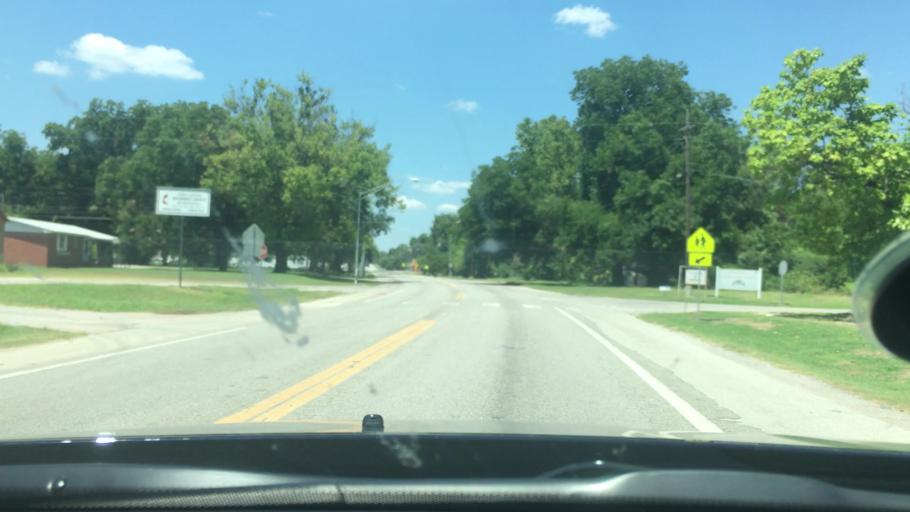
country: US
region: Oklahoma
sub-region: Carter County
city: Dickson
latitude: 34.1862
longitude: -96.8760
